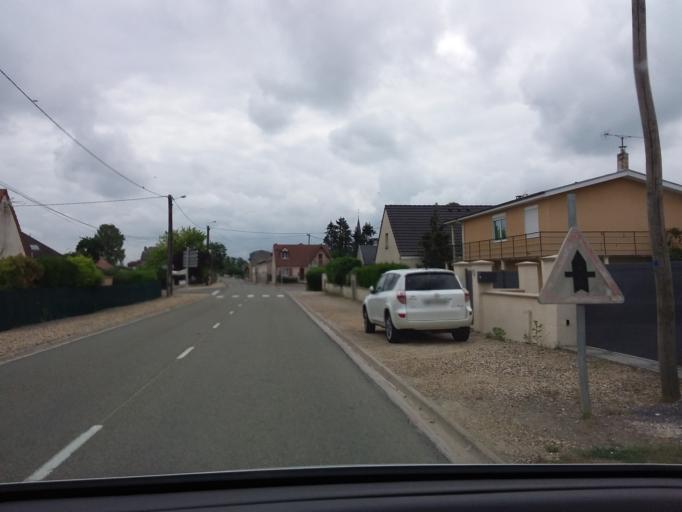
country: FR
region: Champagne-Ardenne
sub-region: Departement de la Marne
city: Cormicy
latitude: 49.4076
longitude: 3.8182
